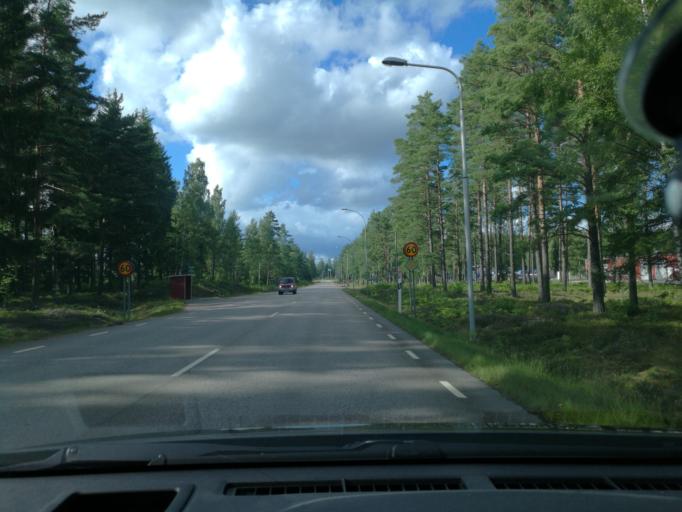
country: SE
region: Kronoberg
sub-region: Vaxjo Kommun
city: Braas
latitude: 57.0554
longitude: 15.0594
